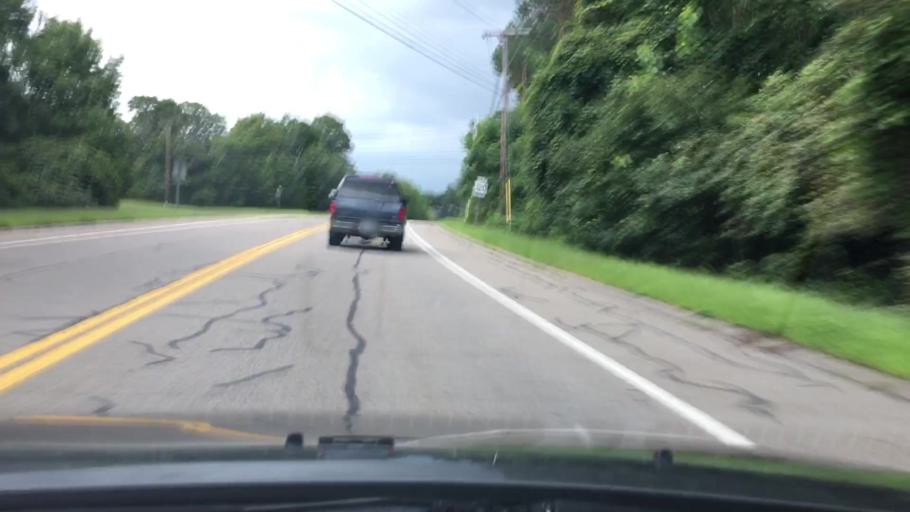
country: US
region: Massachusetts
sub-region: Norfolk County
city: Plainville
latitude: 41.9672
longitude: -71.3486
